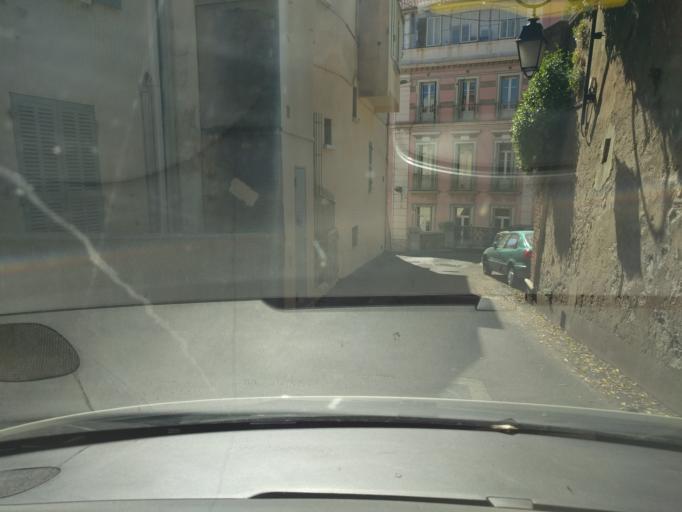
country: FR
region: Provence-Alpes-Cote d'Azur
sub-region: Departement du Var
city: Hyeres
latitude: 43.1199
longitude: 6.1250
